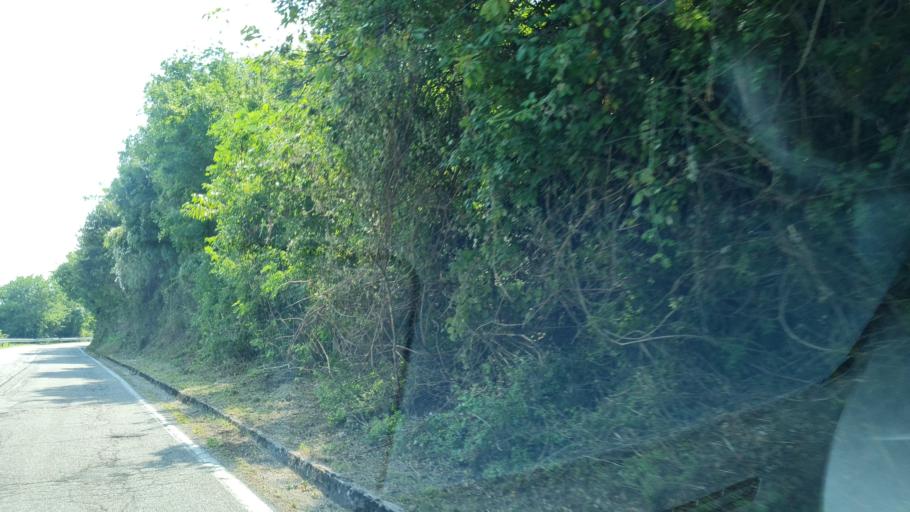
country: IT
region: Veneto
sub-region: Provincia di Vicenza
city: Conco
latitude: 45.7881
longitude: 11.6397
